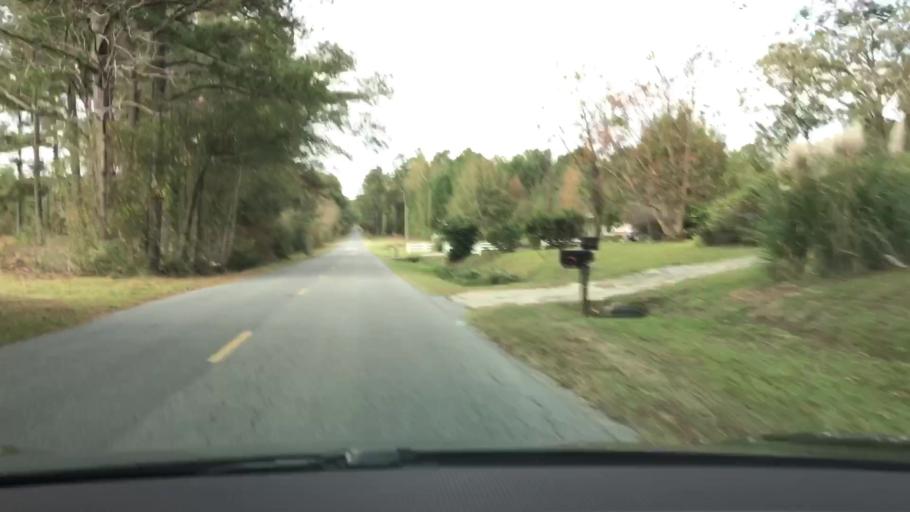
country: US
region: Georgia
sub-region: Jefferson County
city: Wadley
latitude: 32.7994
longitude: -82.3523
